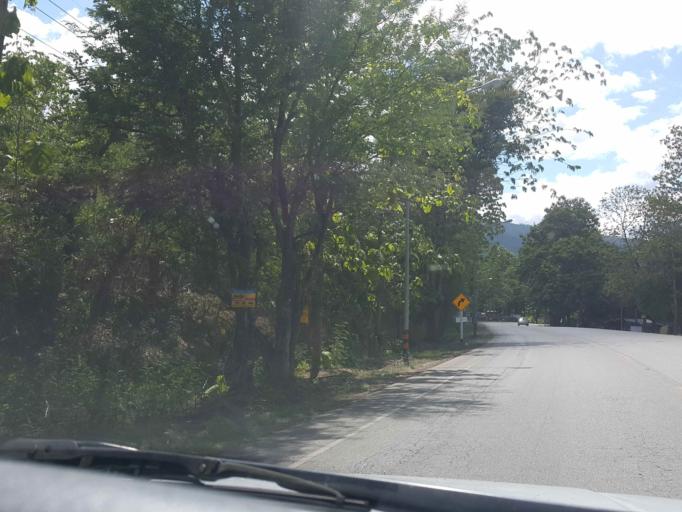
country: TH
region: Chiang Mai
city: Chom Thong
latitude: 18.4776
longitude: 98.6749
